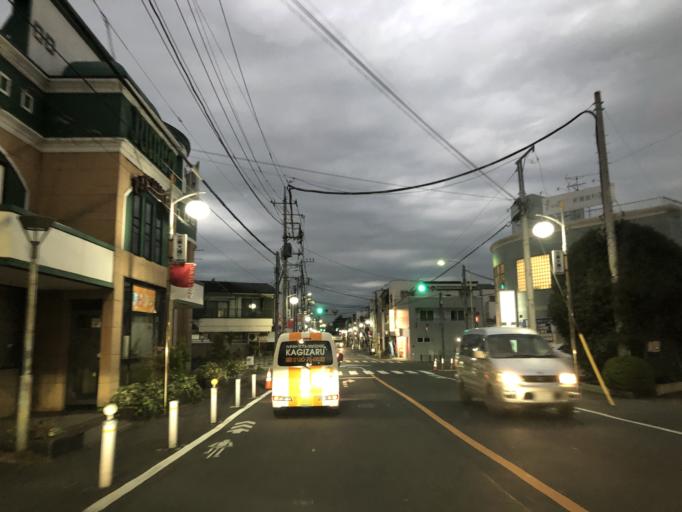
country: JP
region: Tokyo
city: Hino
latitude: 35.6991
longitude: 139.4294
